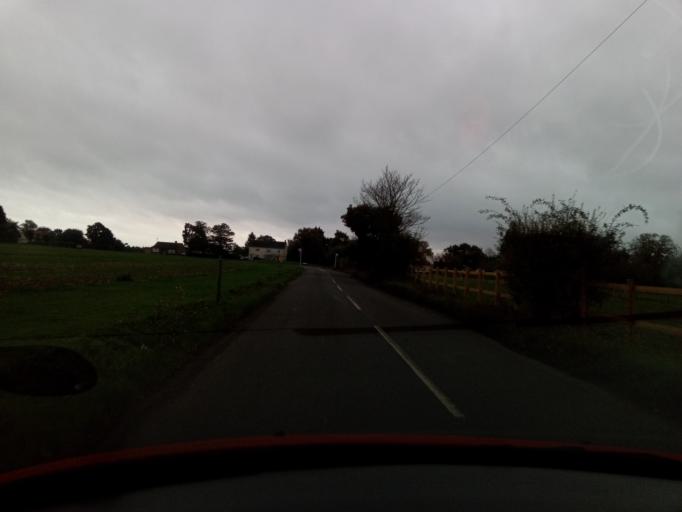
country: GB
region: England
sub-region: Essex
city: West Mersea
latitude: 51.7861
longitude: 0.9394
